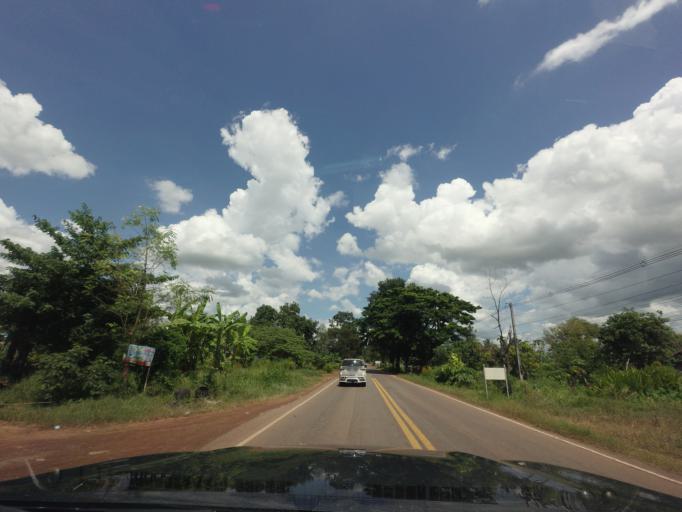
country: TH
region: Changwat Udon Thani
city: Ban Dung
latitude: 17.6668
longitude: 103.1627
